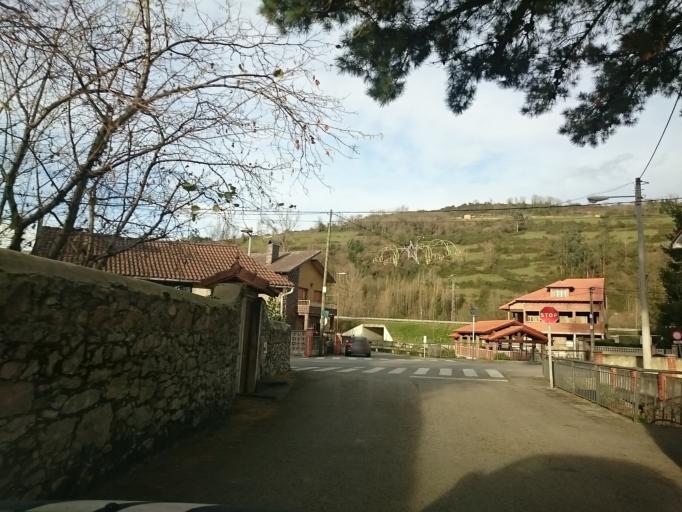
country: ES
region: Asturias
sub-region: Province of Asturias
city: Oviedo
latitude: 43.3205
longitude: -5.8013
